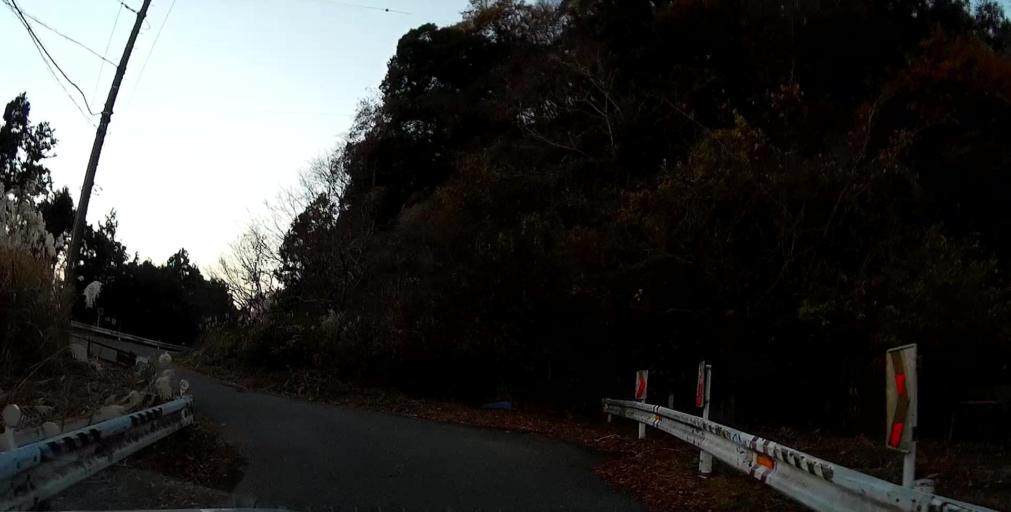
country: JP
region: Yamanashi
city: Uenohara
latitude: 35.5773
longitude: 139.1840
